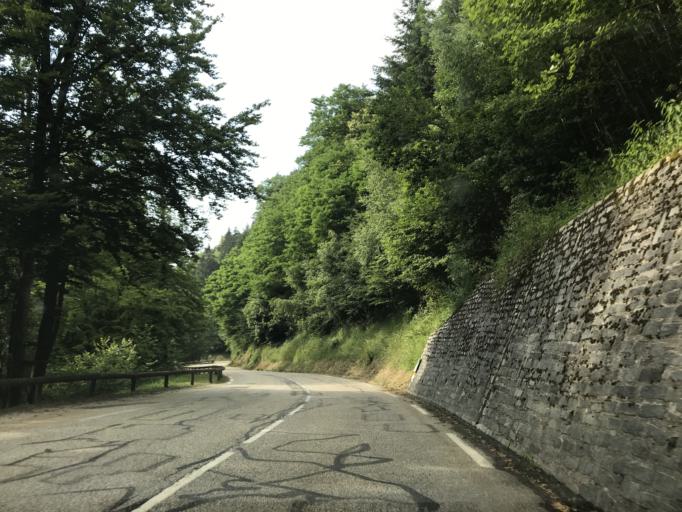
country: FR
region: Rhone-Alpes
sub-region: Departement de l'Isere
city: Allevard
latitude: 45.3733
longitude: 6.0963
